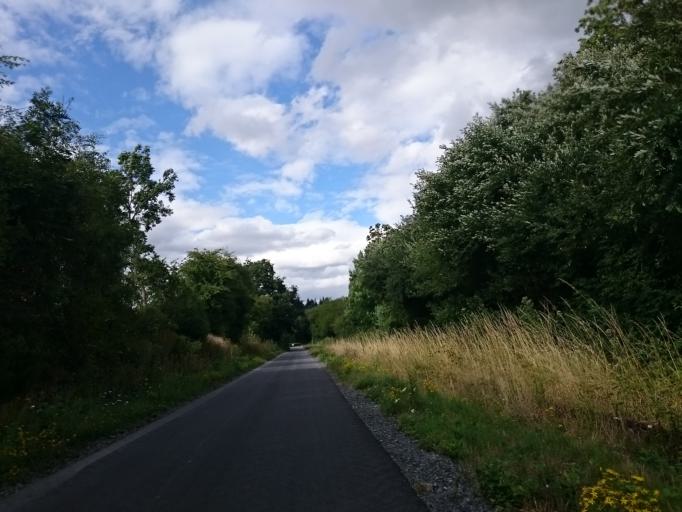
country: FR
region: Lower Normandy
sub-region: Departement du Calvados
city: Thury-Harcourt
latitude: 49.0157
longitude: -0.4690
